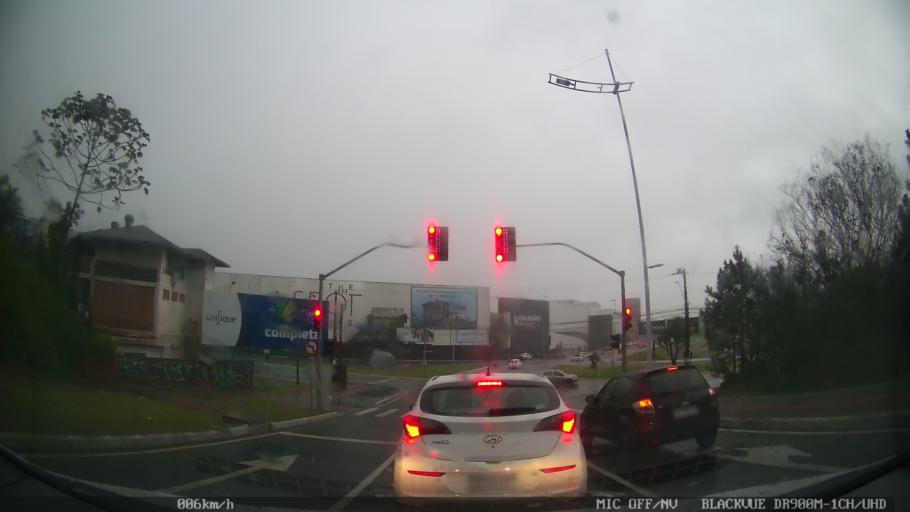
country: BR
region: Santa Catarina
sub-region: Balneario Camboriu
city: Balneario Camboriu
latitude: -26.9909
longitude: -48.6457
